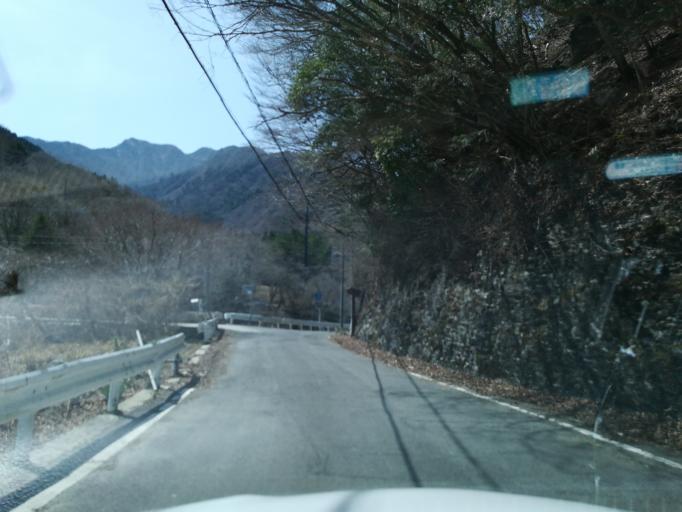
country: JP
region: Tokushima
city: Wakimachi
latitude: 33.8525
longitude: 134.0243
